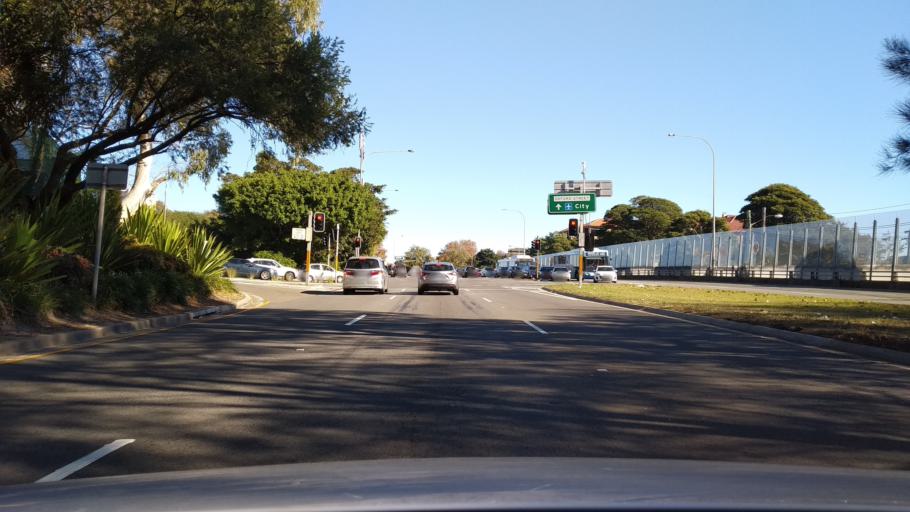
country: AU
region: New South Wales
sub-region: Waverley
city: Bondi Junction
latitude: -33.8898
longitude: 151.2423
